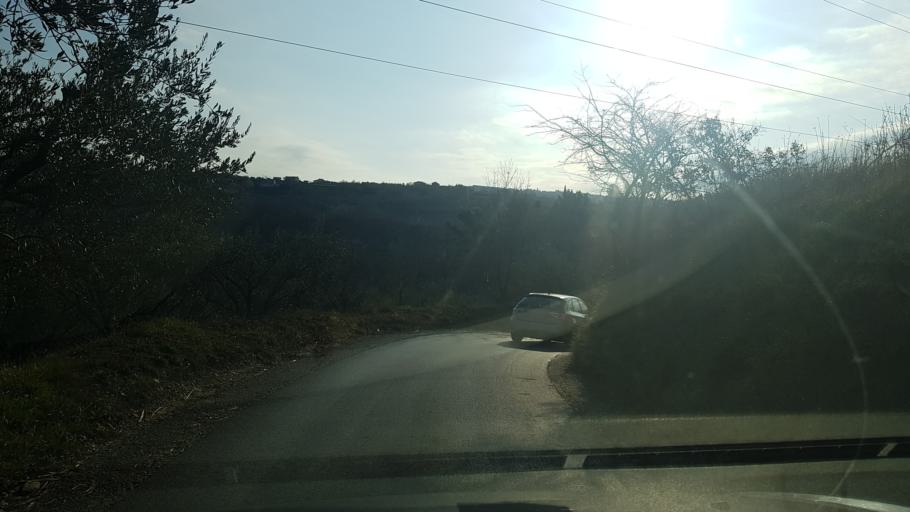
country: SI
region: Koper-Capodistria
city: Prade
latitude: 45.5332
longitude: 13.7776
